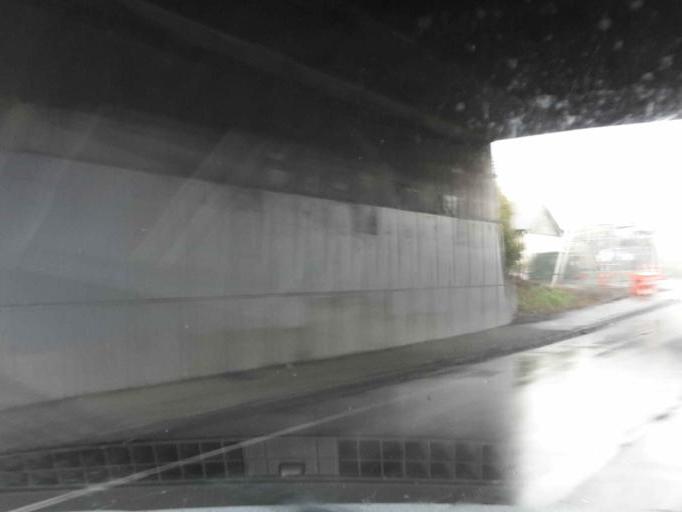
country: NZ
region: Canterbury
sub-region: Selwyn District
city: Prebbleton
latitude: -43.5408
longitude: 172.5508
